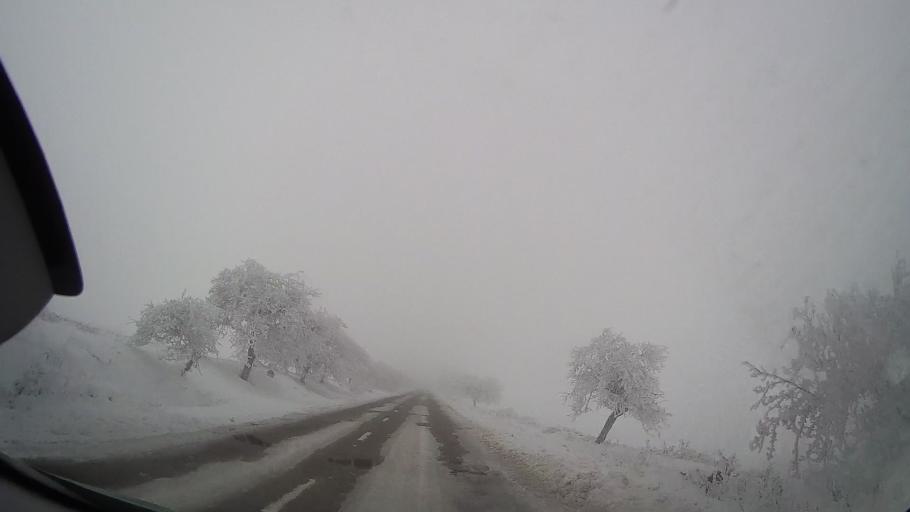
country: RO
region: Neamt
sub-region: Comuna Valea Ursului
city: Valea Ursului
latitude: 46.8306
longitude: 27.0670
